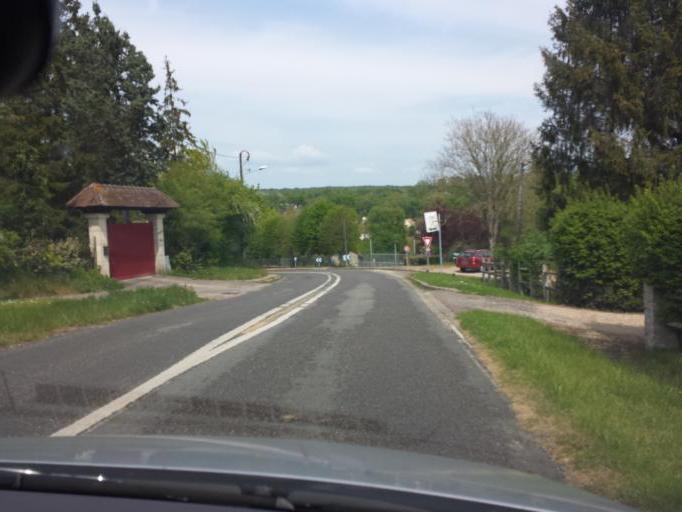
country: FR
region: Ile-de-France
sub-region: Departement des Yvelines
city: Septeuil
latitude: 48.8886
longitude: 1.6765
